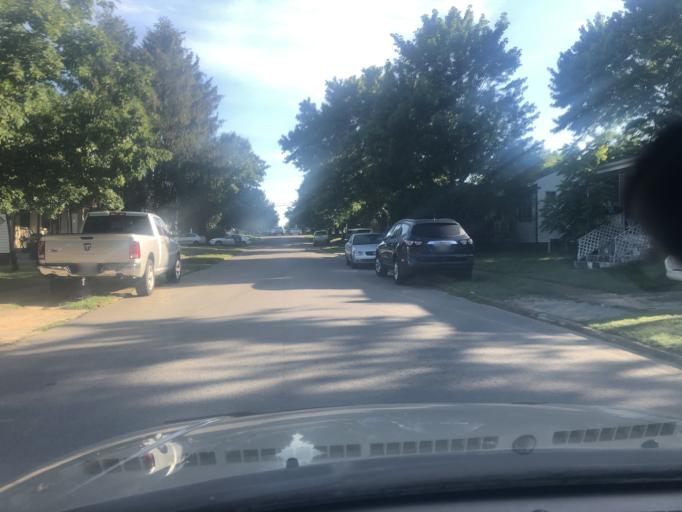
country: US
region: Tennessee
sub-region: Davidson County
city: Lakewood
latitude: 36.2566
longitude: -86.6497
